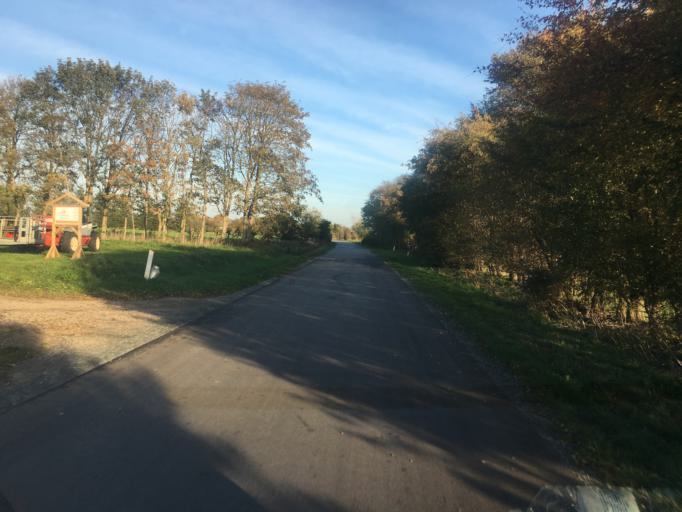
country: DE
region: Schleswig-Holstein
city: Bramstedtlund
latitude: 54.8941
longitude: 9.0556
